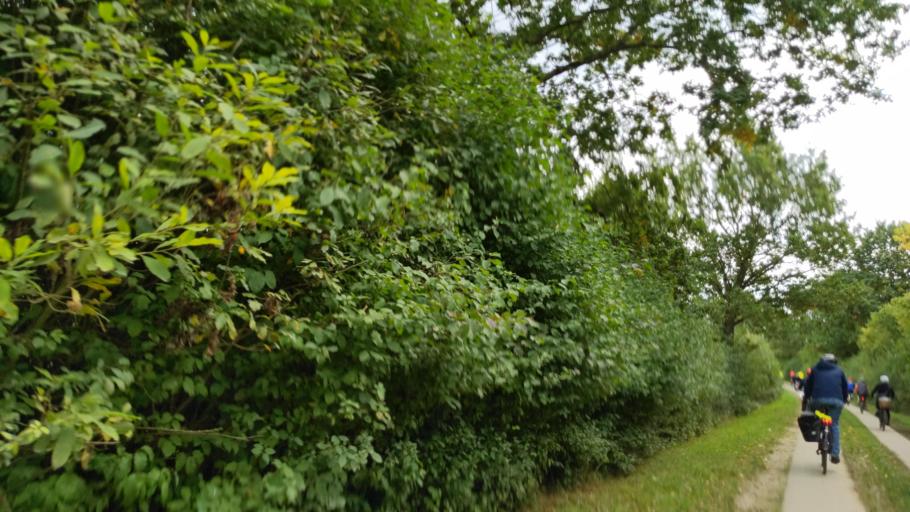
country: DE
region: Mecklenburg-Vorpommern
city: Schlagsdorf
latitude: 53.7326
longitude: 10.8150
